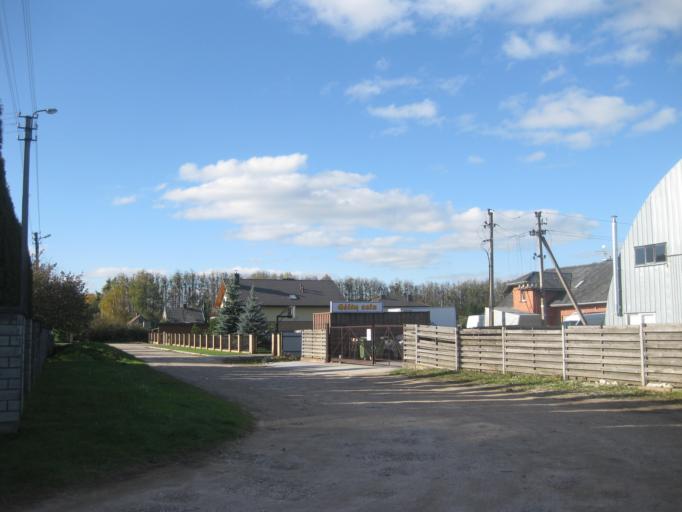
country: LT
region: Kauno apskritis
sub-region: Kauno rajonas
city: Garliava
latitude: 54.8414
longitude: 23.8827
